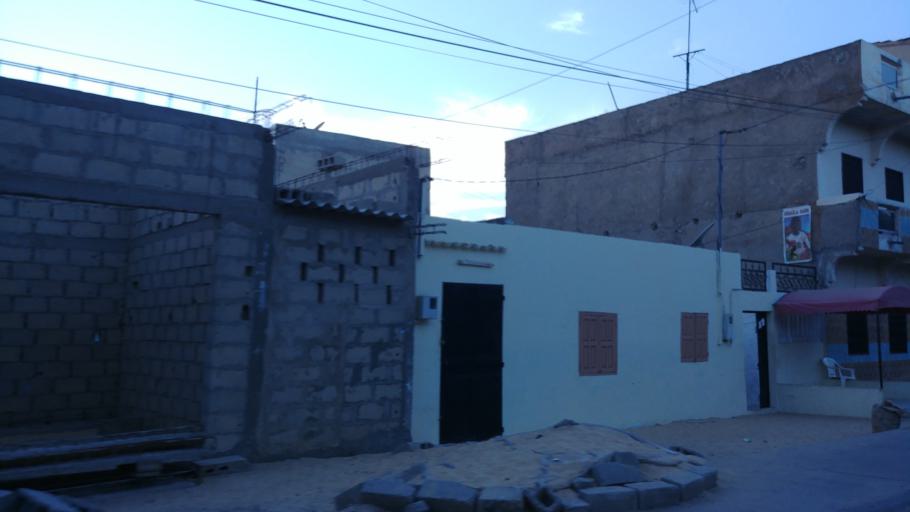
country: SN
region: Saint-Louis
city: Saint-Louis
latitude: 16.0157
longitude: -16.4898
